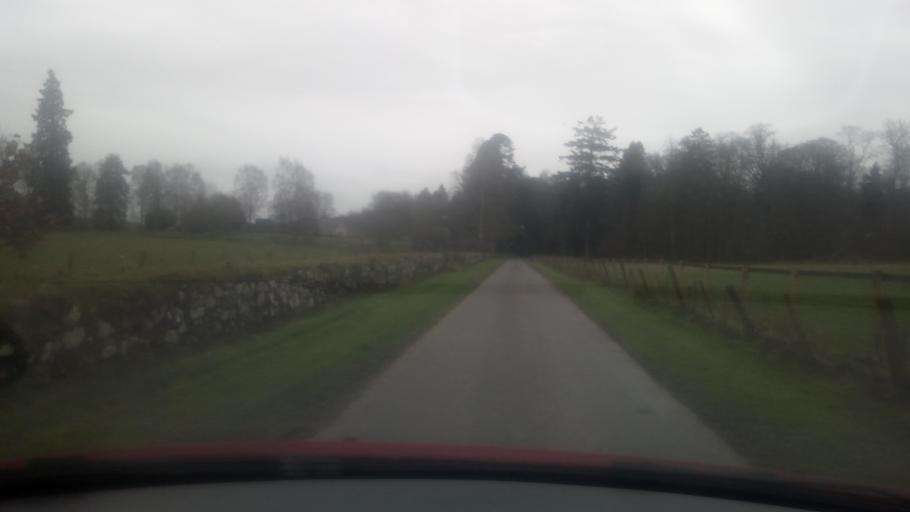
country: GB
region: Scotland
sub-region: The Scottish Borders
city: Jedburgh
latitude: 55.4474
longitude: -2.6402
